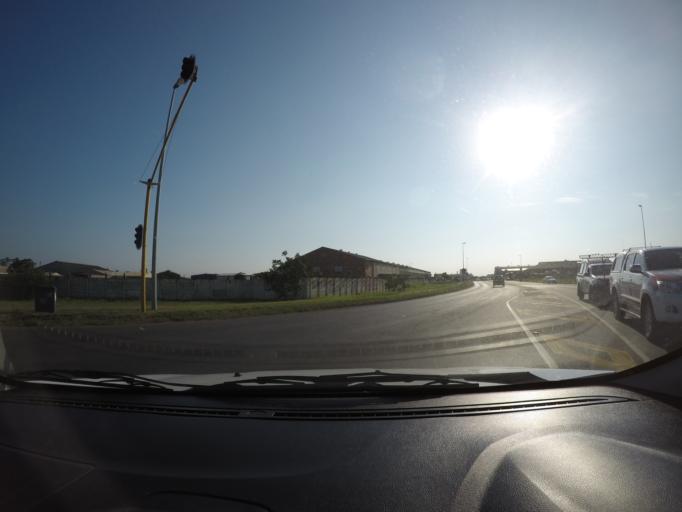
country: ZA
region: KwaZulu-Natal
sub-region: uThungulu District Municipality
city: Richards Bay
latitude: -28.7518
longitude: 32.0299
